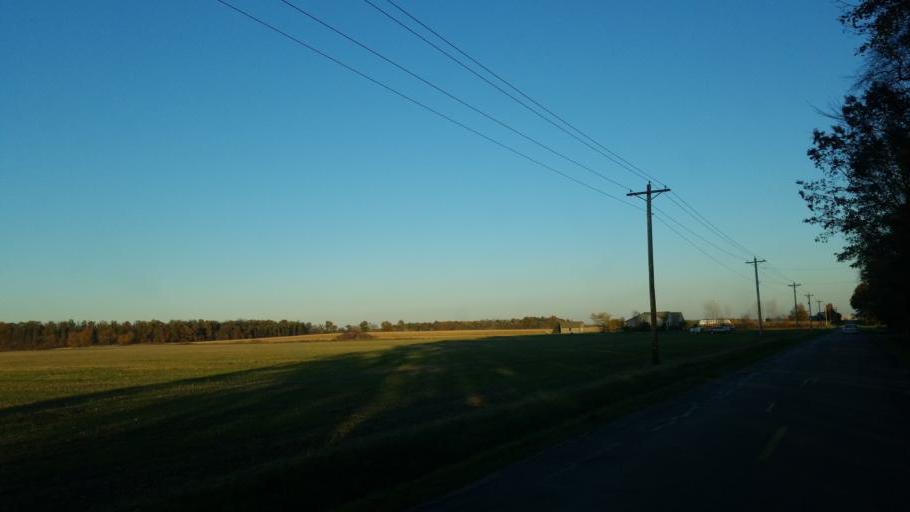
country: US
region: Ohio
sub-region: Sandusky County
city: Mount Carmel
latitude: 41.2123
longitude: -82.9513
